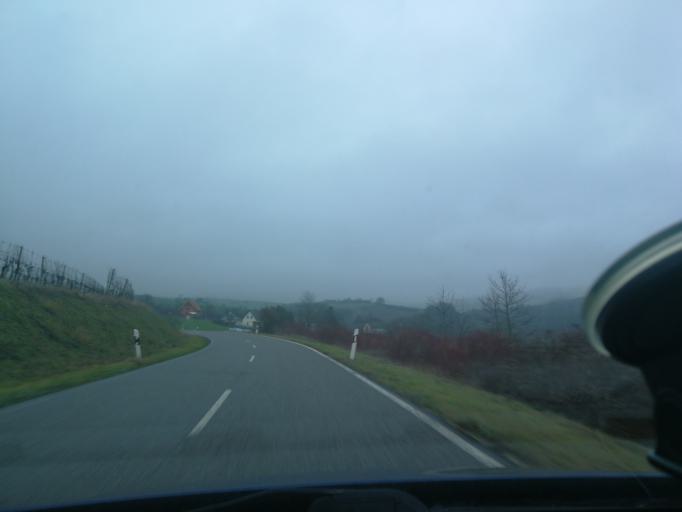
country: DE
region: Rheinland-Pfalz
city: Oberbillig
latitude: 49.7415
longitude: 6.5166
